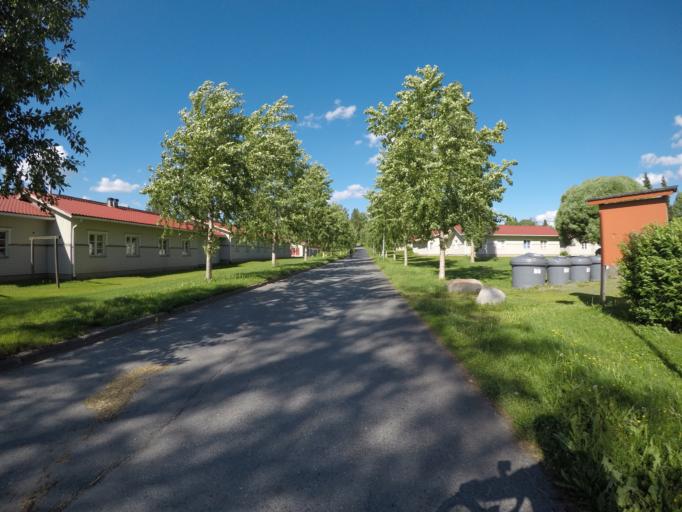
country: FI
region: Haeme
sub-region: Haemeenlinna
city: Haemeenlinna
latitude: 60.9807
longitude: 24.4735
